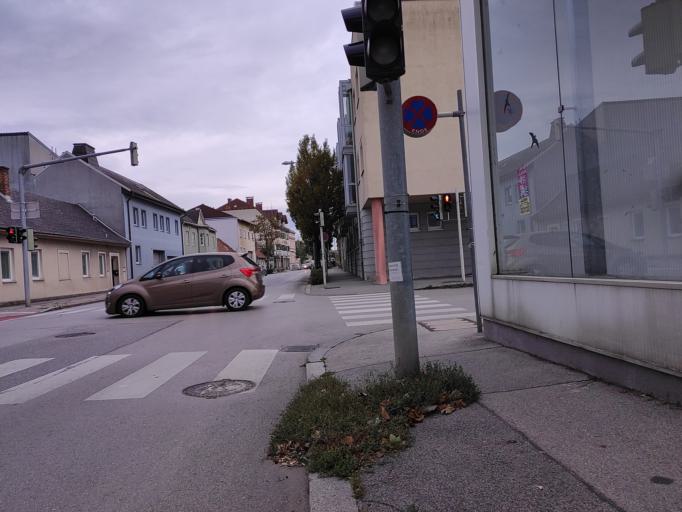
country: AT
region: Lower Austria
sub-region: Politischer Bezirk Baden
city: Baden
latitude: 47.9998
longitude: 16.2298
